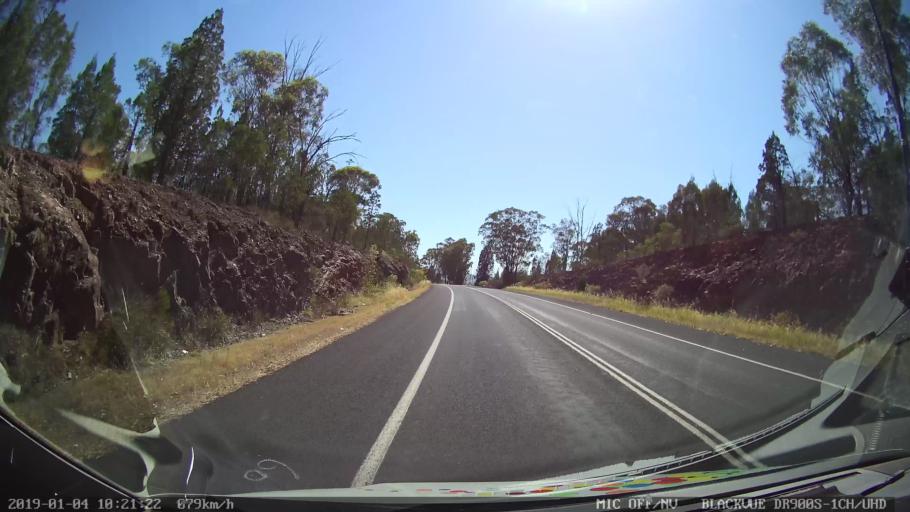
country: AU
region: New South Wales
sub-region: Cabonne
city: Canowindra
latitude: -33.3732
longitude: 148.5096
